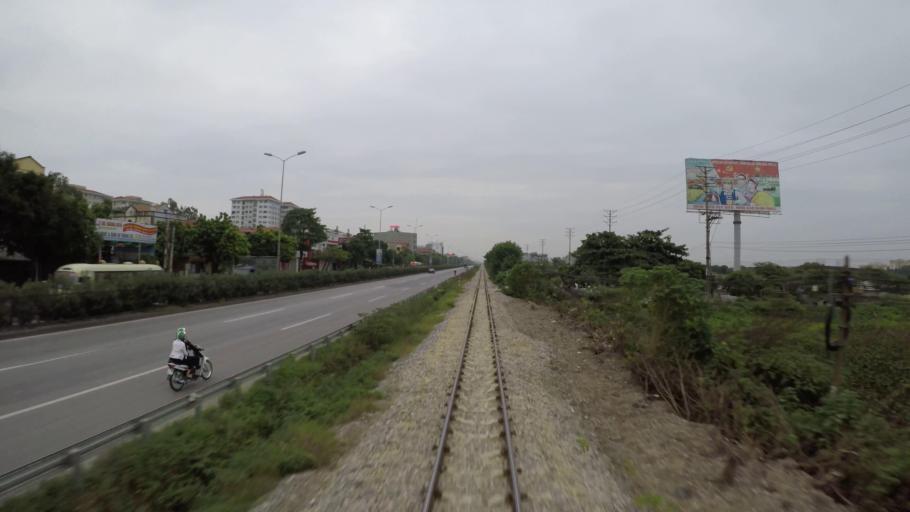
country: VN
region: Hung Yen
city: Nhu Quynh
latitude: 20.9844
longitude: 105.9786
